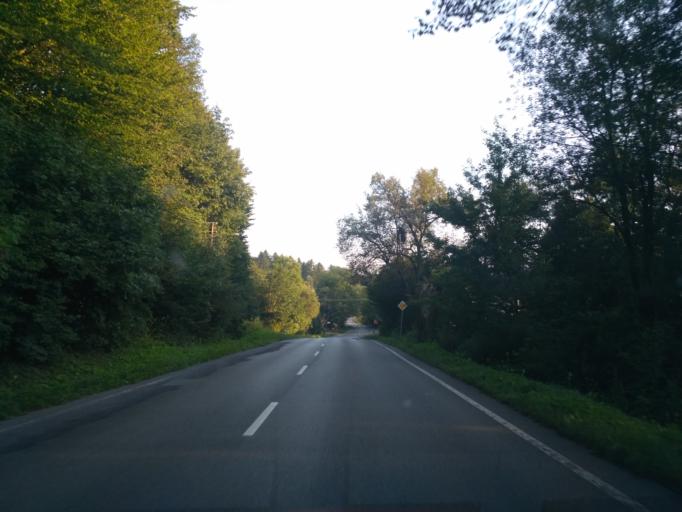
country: SK
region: Presovsky
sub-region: Okres Presov
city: Presov
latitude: 48.9853
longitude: 21.1754
